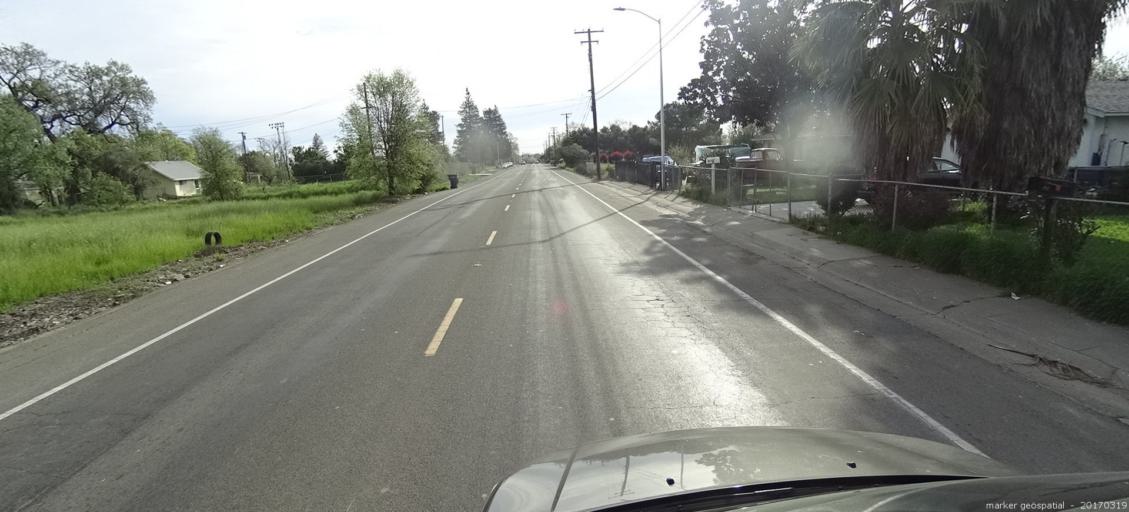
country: US
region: California
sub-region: Sacramento County
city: Sacramento
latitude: 38.6302
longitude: -121.4617
